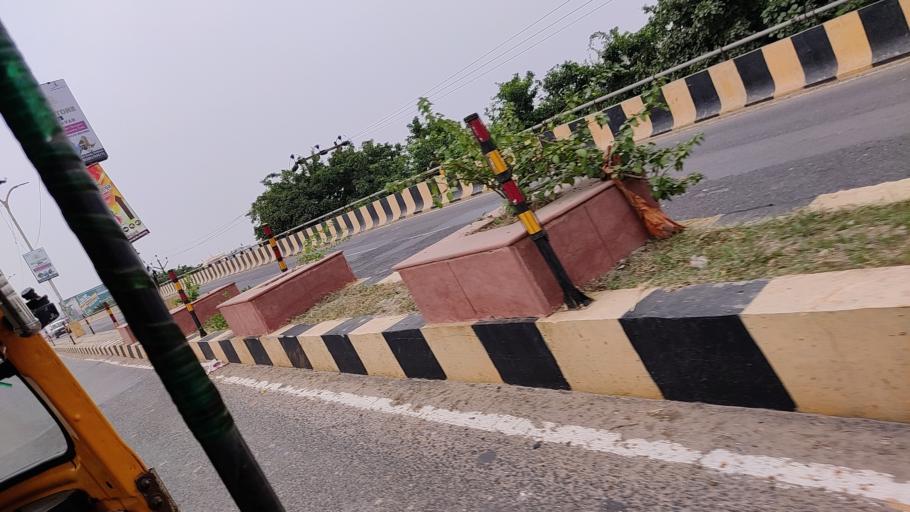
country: IN
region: Uttar Pradesh
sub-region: Mathura
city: Vrindavan
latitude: 27.5627
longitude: 77.6810
